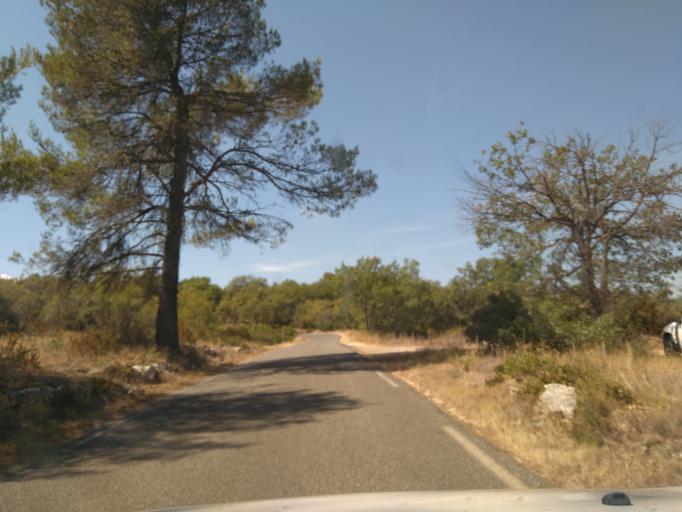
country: FR
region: Provence-Alpes-Cote d'Azur
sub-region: Departement du Var
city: Regusse
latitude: 43.7112
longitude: 6.0854
